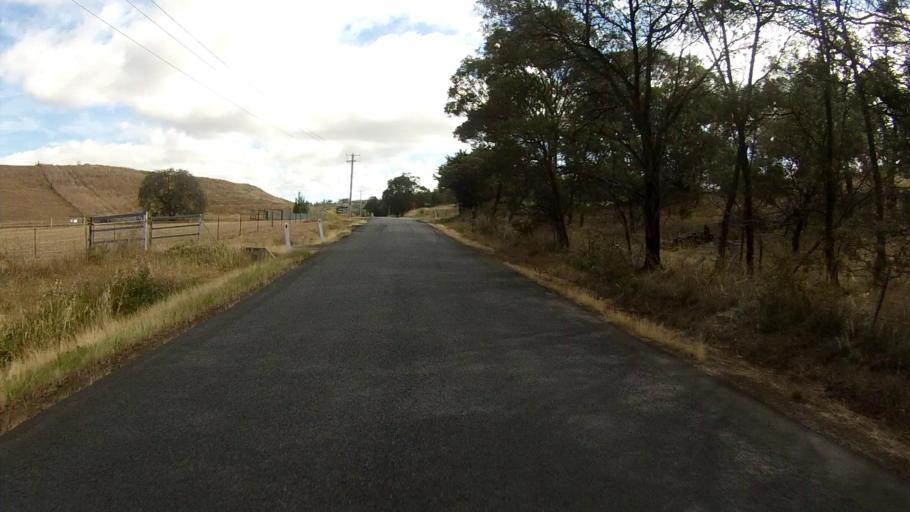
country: AU
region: Tasmania
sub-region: Brighton
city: Old Beach
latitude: -42.7472
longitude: 147.3009
